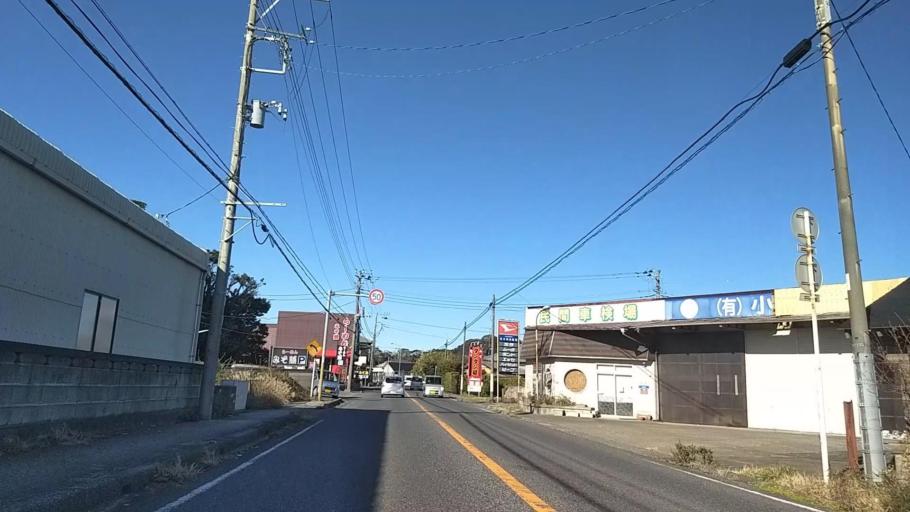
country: JP
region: Chiba
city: Ohara
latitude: 35.3211
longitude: 140.4028
